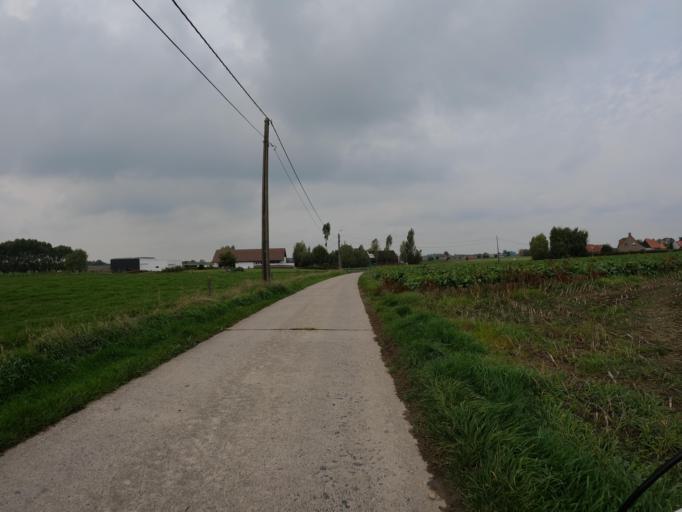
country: BE
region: Flanders
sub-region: Provincie West-Vlaanderen
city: Ruiselede
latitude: 51.0244
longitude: 3.3650
